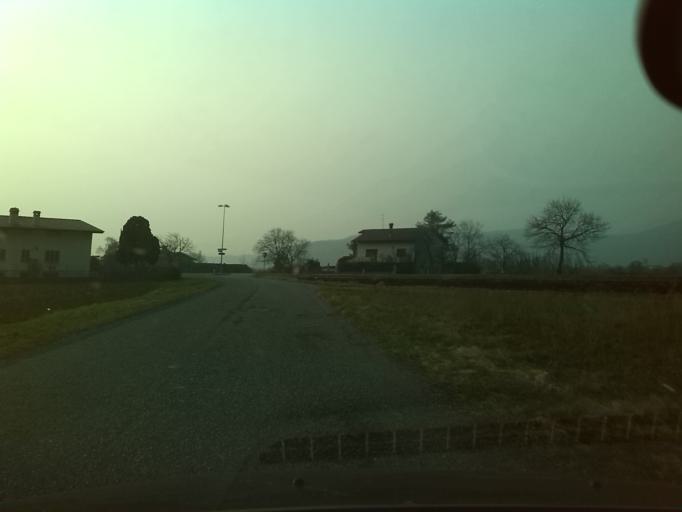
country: IT
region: Friuli Venezia Giulia
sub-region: Provincia di Udine
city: San Pietro al Natisone
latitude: 46.0997
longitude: 13.4648
